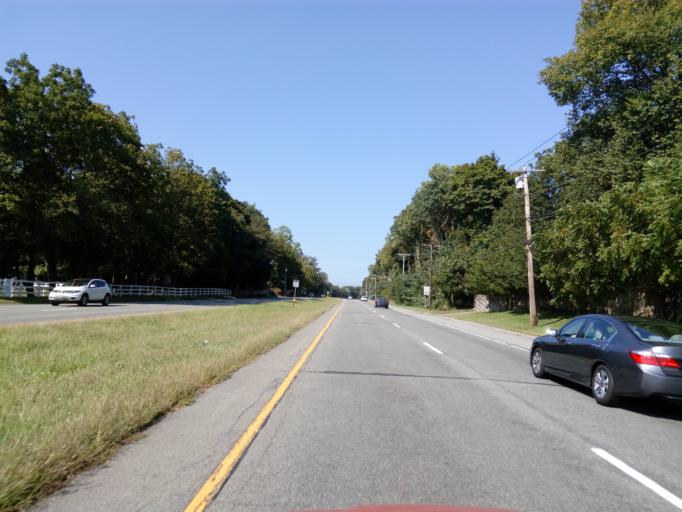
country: US
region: New York
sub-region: Nassau County
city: Jericho
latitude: 40.8011
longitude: -73.5375
